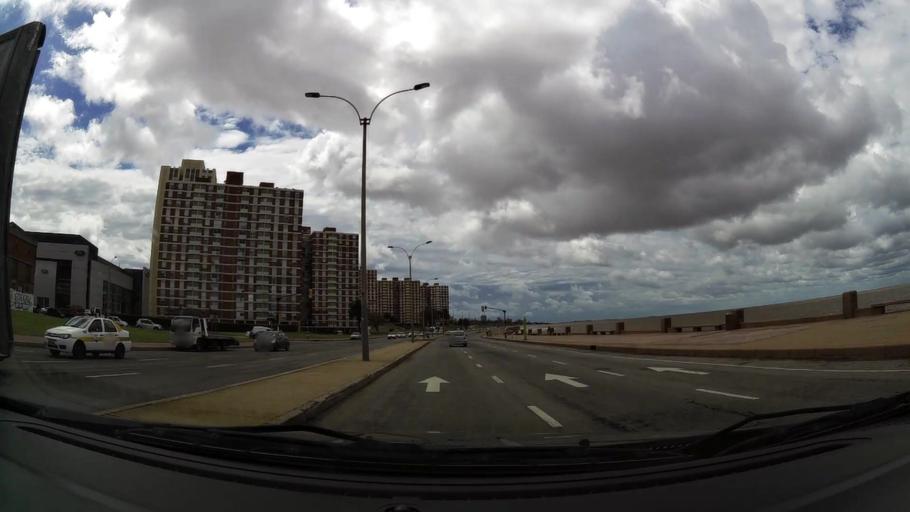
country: UY
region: Montevideo
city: Montevideo
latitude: -34.9126
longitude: -56.1937
